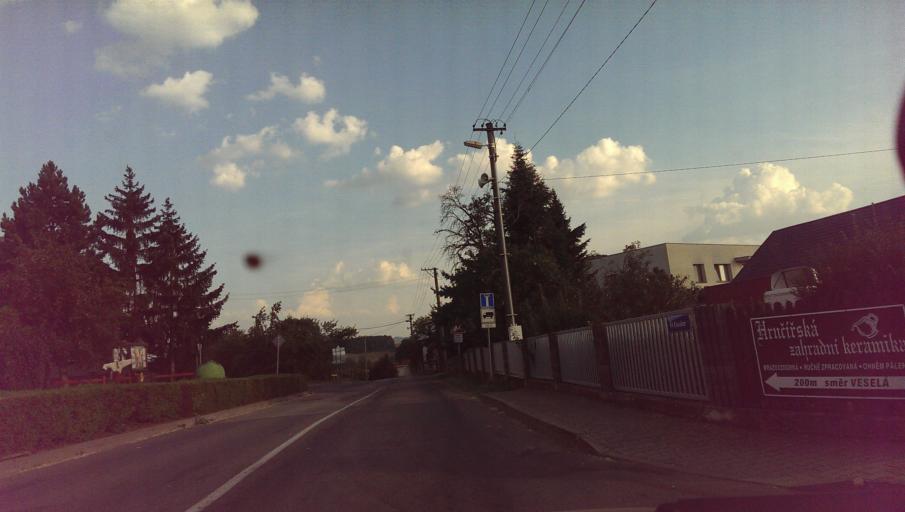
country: CZ
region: Zlin
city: Hvozdna
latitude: 49.2569
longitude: 17.7565
